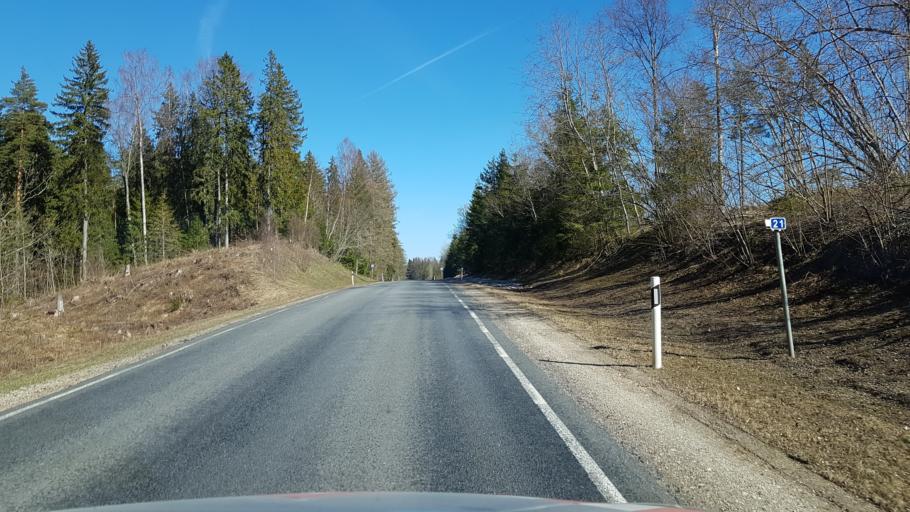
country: EE
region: Laeaene-Virumaa
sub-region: Vinni vald
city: Vinni
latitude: 59.2730
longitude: 26.6380
